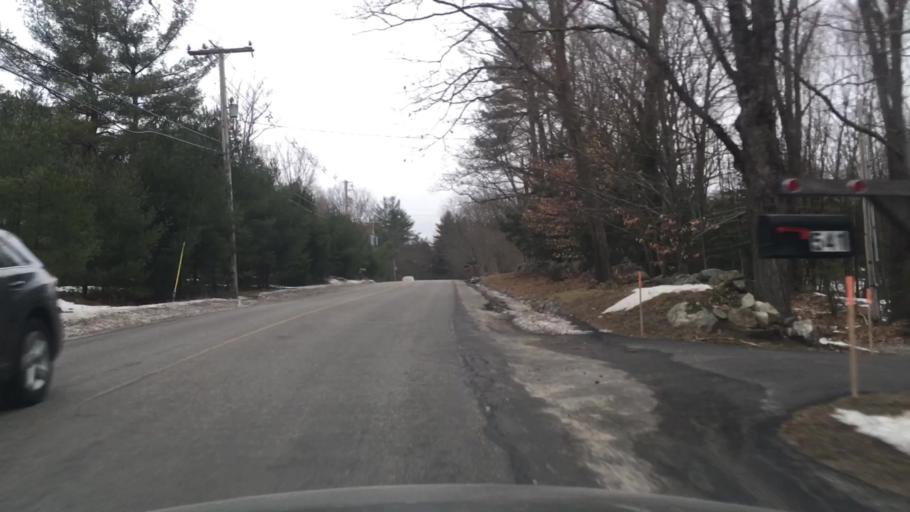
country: US
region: New Hampshire
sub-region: Hillsborough County
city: Goffstown
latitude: 42.9715
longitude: -71.6339
